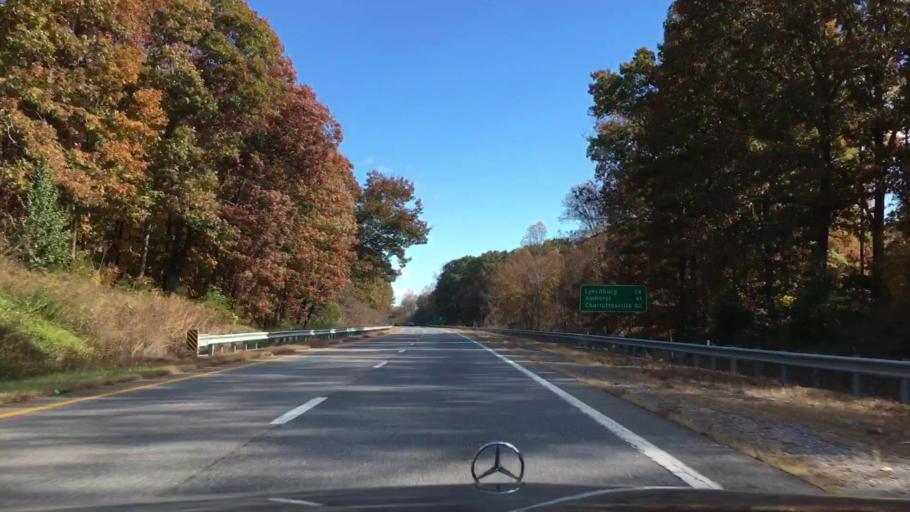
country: US
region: Virginia
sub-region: Campbell County
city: Altavista
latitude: 37.1367
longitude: -79.2792
